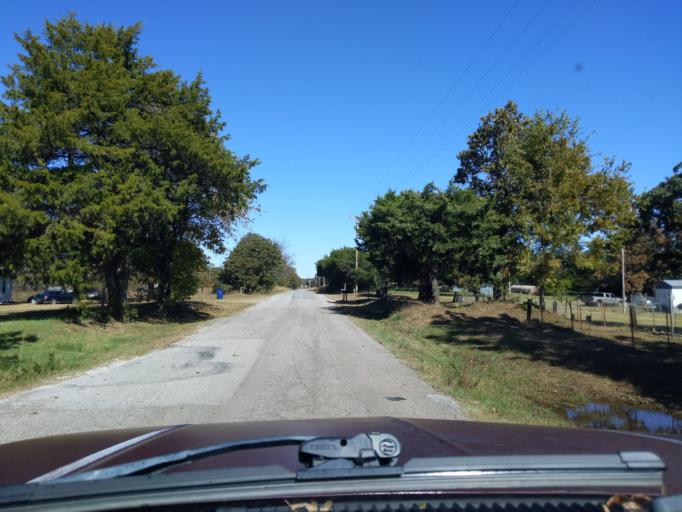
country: US
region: Oklahoma
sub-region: Creek County
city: Bristow
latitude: 35.6988
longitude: -96.4100
